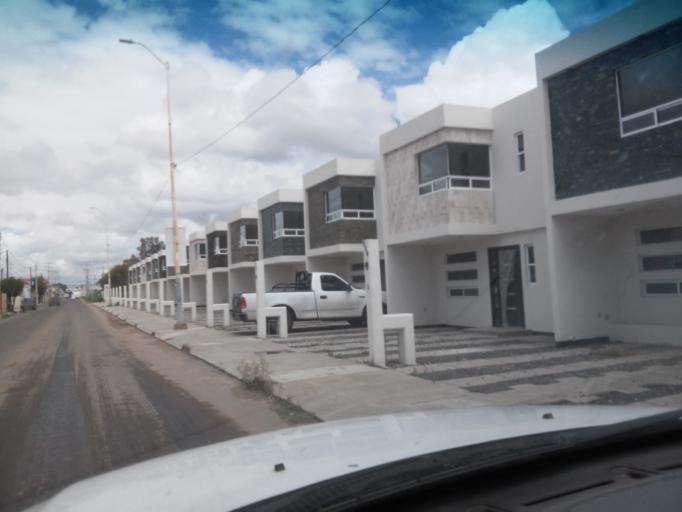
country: MX
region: Durango
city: Victoria de Durango
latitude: 24.0273
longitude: -104.6175
